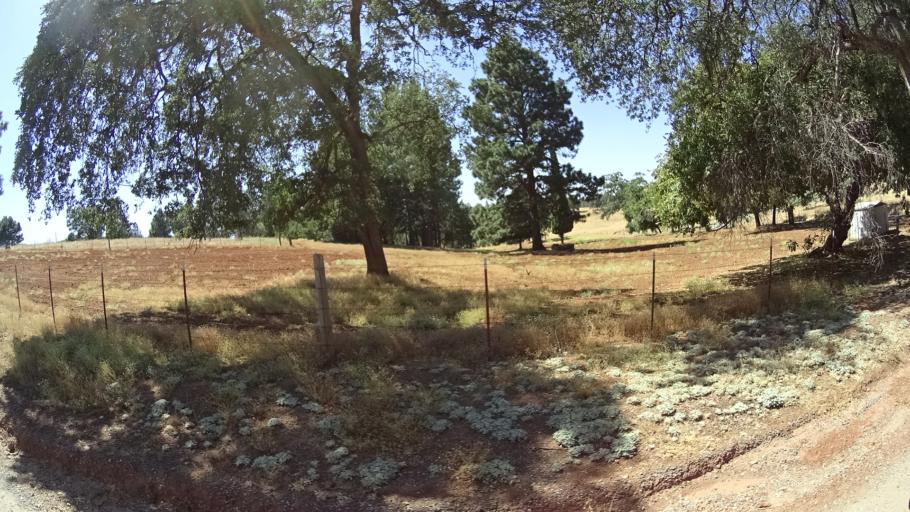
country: US
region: California
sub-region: Calaveras County
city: Mountain Ranch
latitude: 38.2894
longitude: -120.5985
